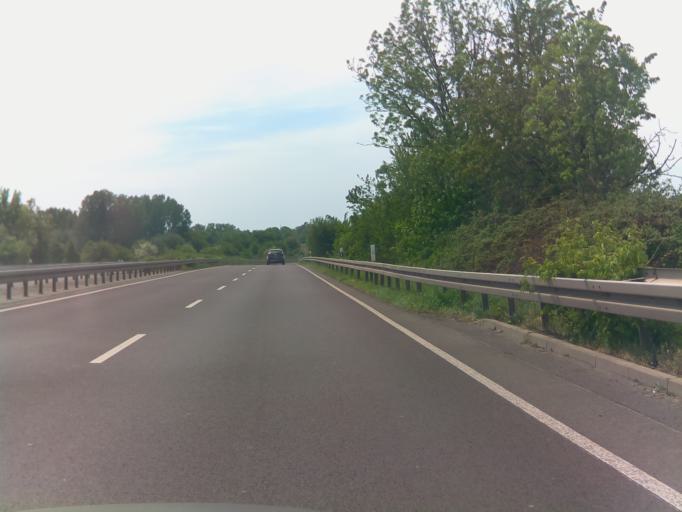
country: DE
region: Saxony-Anhalt
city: Hohendodeleben
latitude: 52.0561
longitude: 11.5414
